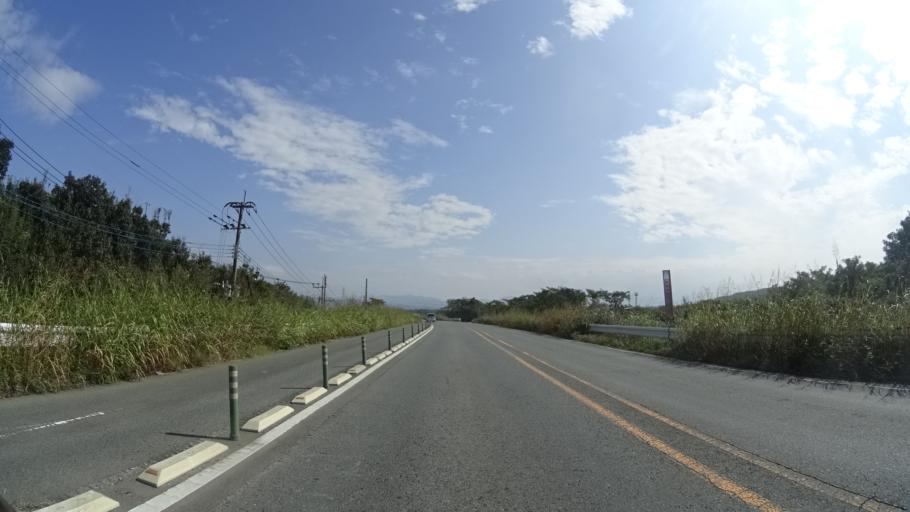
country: JP
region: Kumamoto
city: Kumamoto
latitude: 32.7373
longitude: 130.7430
